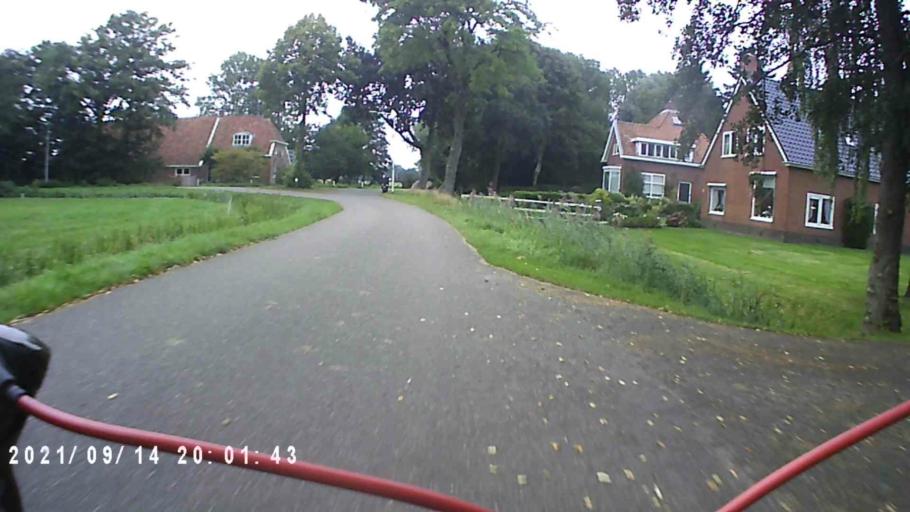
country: NL
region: Groningen
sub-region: Gemeente Haren
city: Haren
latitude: 53.1910
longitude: 6.6028
